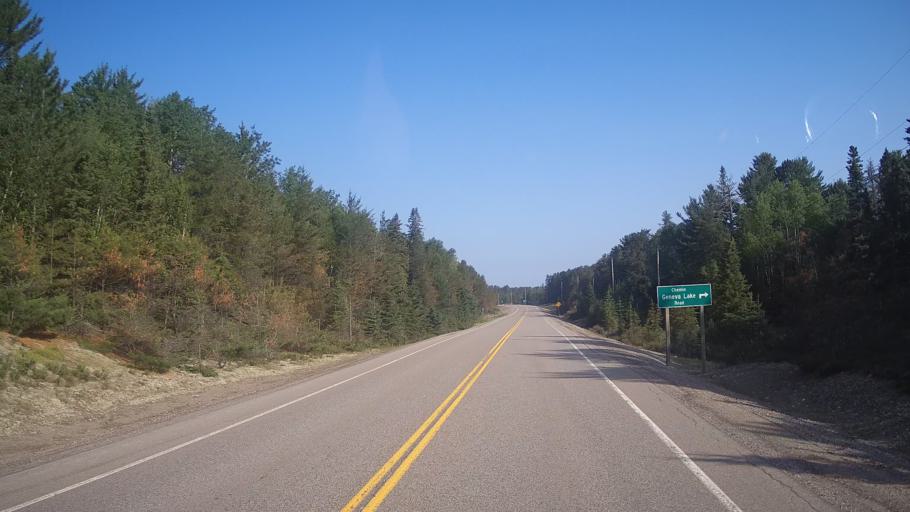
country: CA
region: Ontario
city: Rayside-Balfour
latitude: 46.7153
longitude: -81.5639
